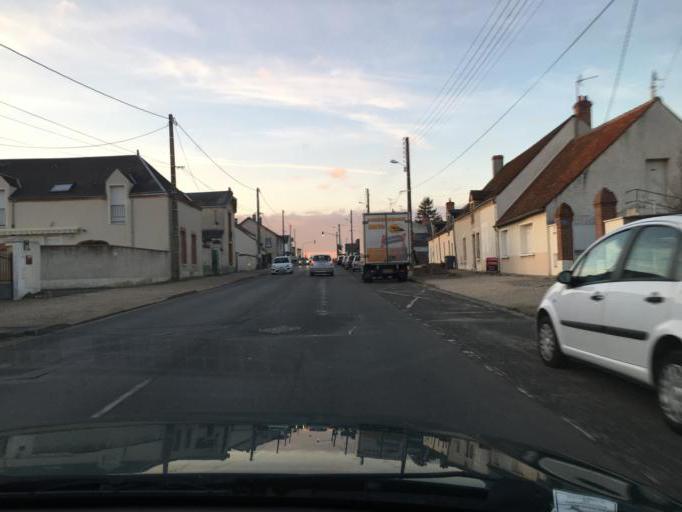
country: FR
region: Centre
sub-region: Departement du Loiret
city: Ingre
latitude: 47.9271
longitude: 1.8429
